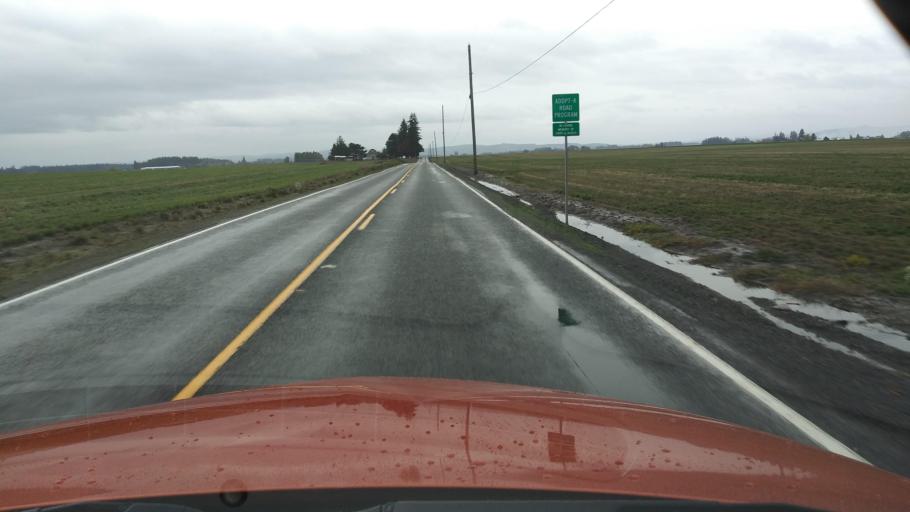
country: US
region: Oregon
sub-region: Washington County
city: North Plains
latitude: 45.5894
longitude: -123.0162
